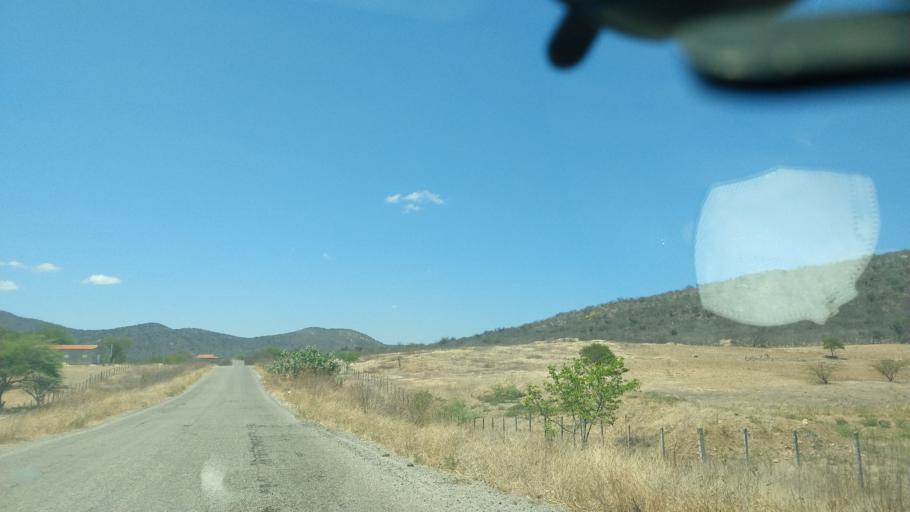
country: BR
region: Rio Grande do Norte
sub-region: Sao Tome
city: Sao Tome
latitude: -5.9745
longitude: -36.1407
